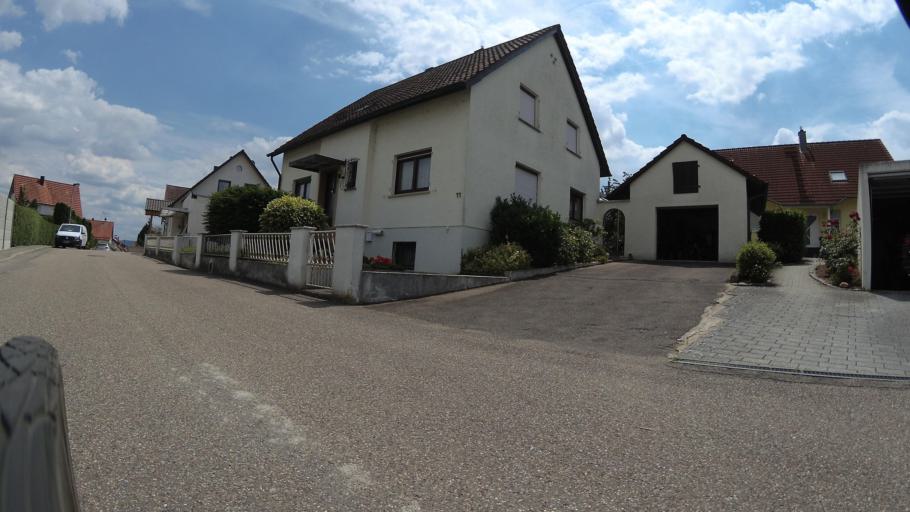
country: DE
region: Baden-Wuerttemberg
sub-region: Regierungsbezirk Stuttgart
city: Neudenau
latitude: 49.2650
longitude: 9.2952
